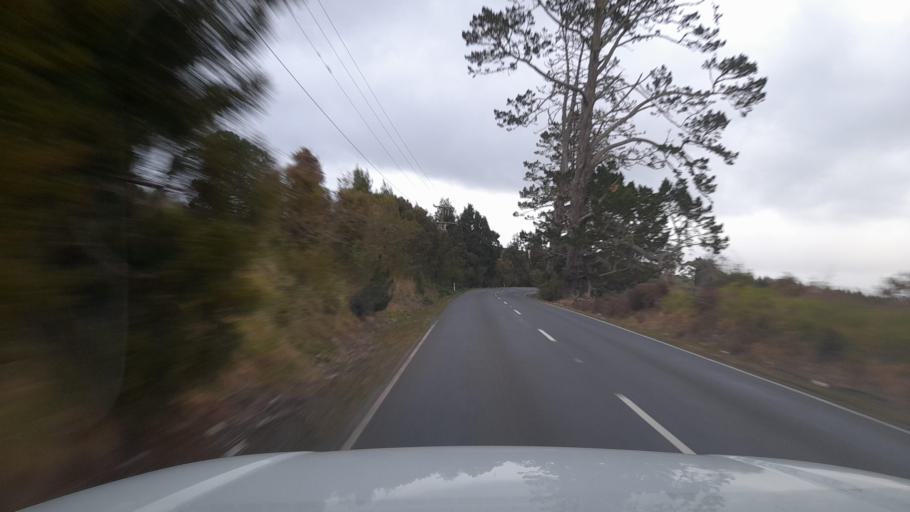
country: NZ
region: Northland
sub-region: Whangarei
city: Maungatapere
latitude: -35.7431
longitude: 174.2044
